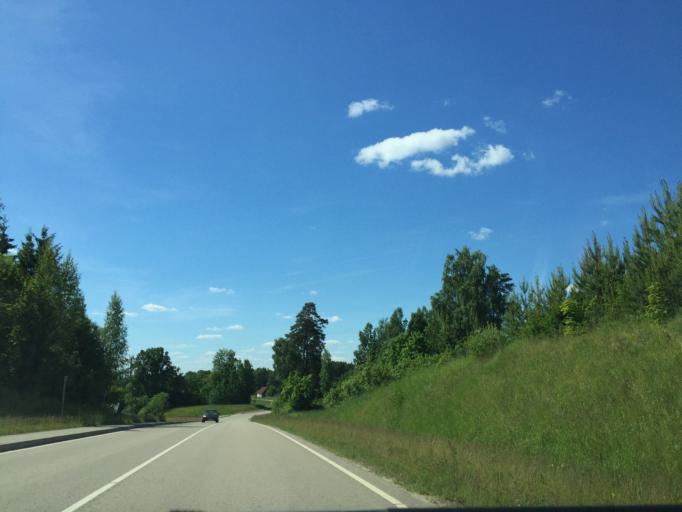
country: LV
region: Preilu Rajons
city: Jaunaglona
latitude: 56.2376
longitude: 27.2235
